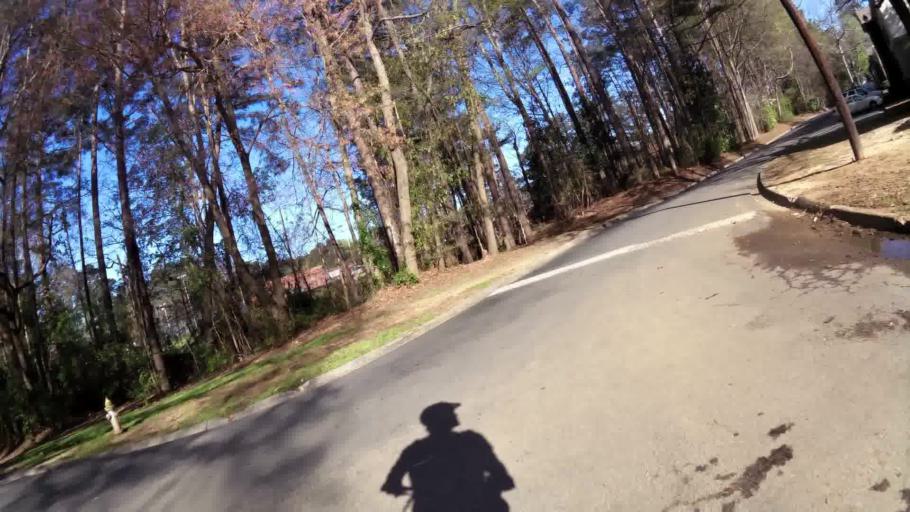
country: US
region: Georgia
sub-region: DeKalb County
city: Clarkston
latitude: 33.8388
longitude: -84.2641
